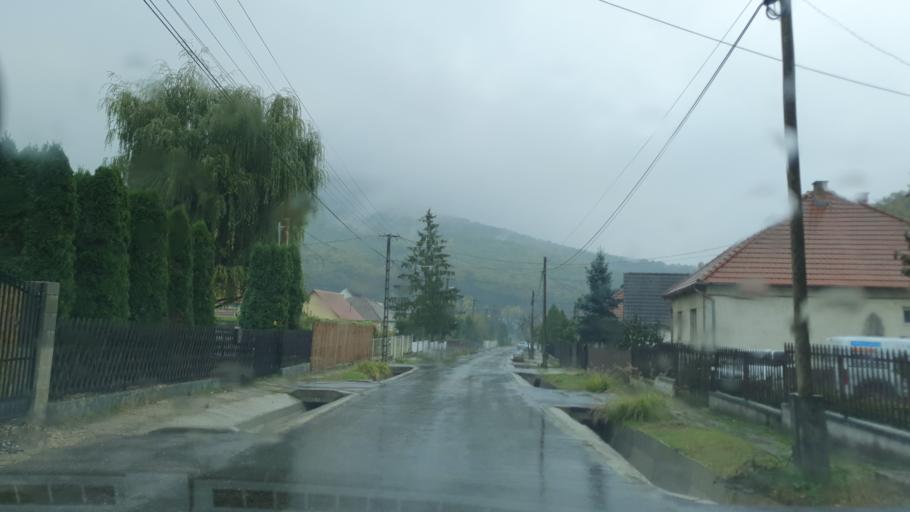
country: HU
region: Pest
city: Veroce
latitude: 47.8457
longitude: 19.0953
